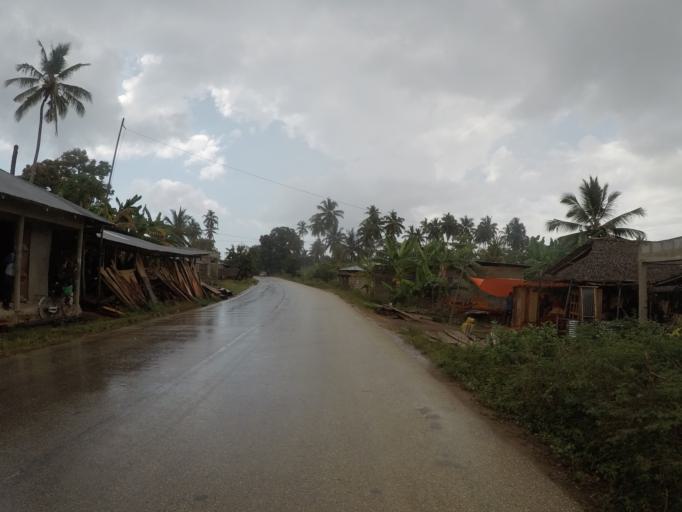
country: TZ
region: Zanzibar North
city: Mkokotoni
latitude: -5.9582
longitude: 39.1948
